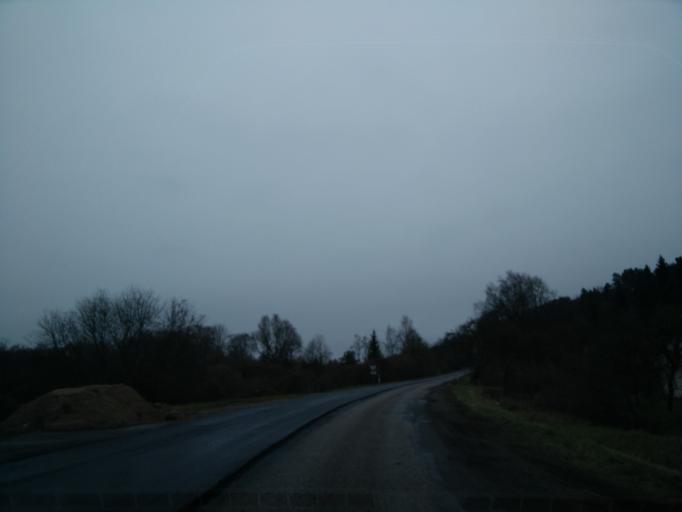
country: LT
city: Ariogala
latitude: 55.2801
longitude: 23.4486
